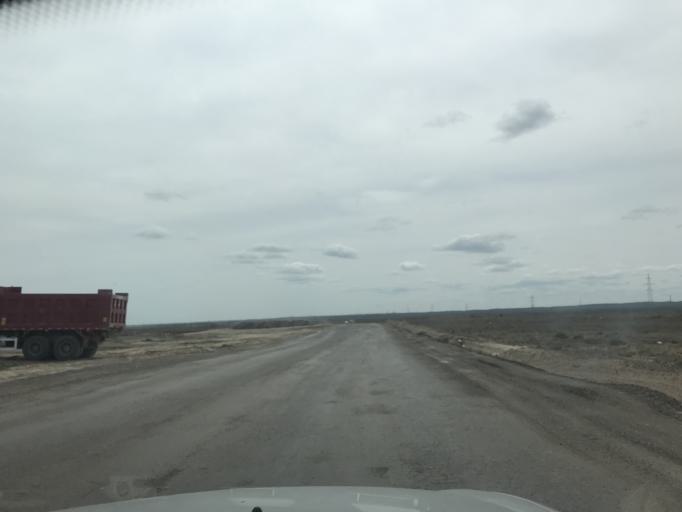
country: KZ
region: Almaty Oblysy
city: Ulken
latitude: 45.2635
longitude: 73.7967
